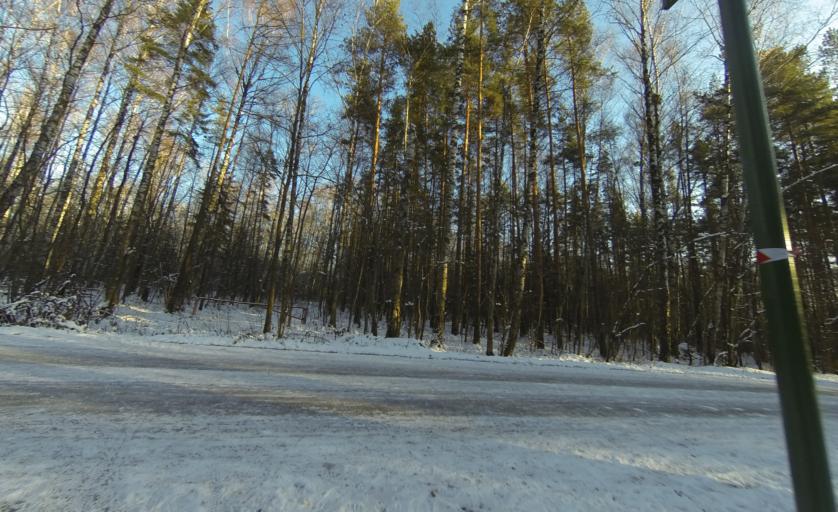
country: RU
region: Moskovskaya
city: Bogorodskoye
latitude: 55.8375
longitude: 37.7271
